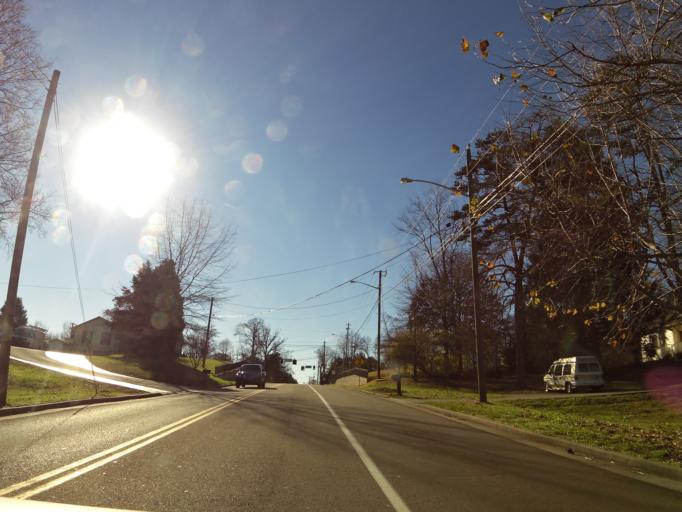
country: US
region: Tennessee
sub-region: Knox County
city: Knoxville
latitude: 36.0256
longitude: -83.9535
